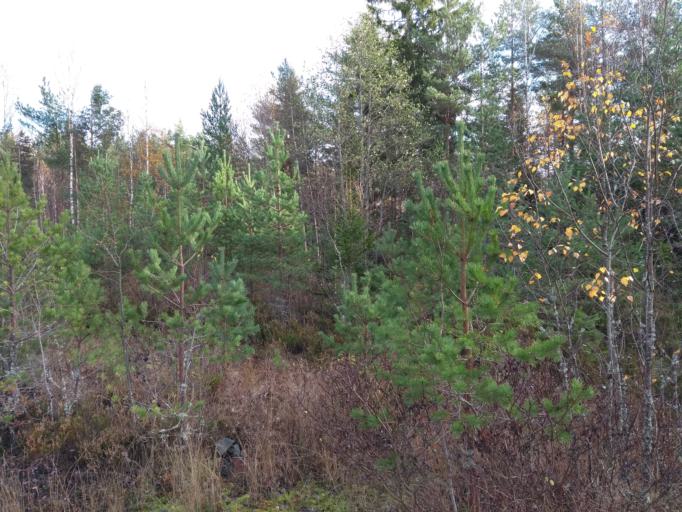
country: SE
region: OEstergoetland
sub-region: Norrkopings Kommun
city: Jursla
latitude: 58.7048
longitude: 16.2500
